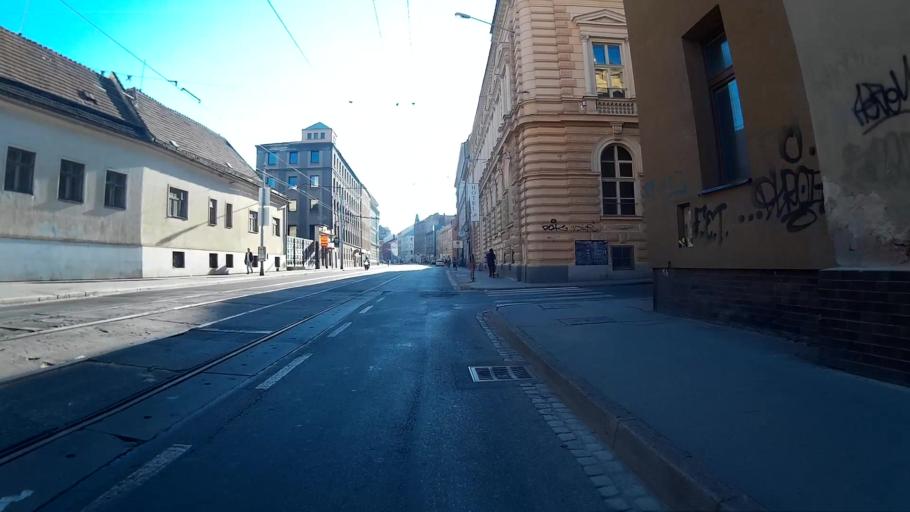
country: CZ
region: South Moravian
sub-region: Mesto Brno
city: Brno
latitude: 49.1989
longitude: 16.6224
